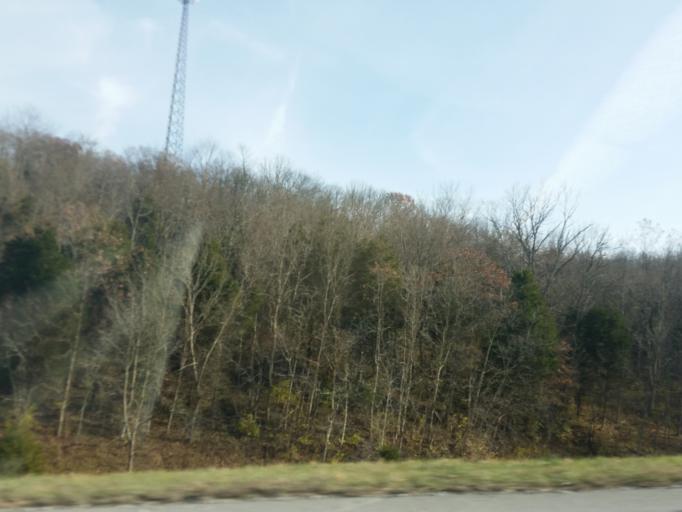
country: US
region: Kentucky
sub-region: Pendleton County
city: Falmouth
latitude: 38.7352
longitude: -84.3700
